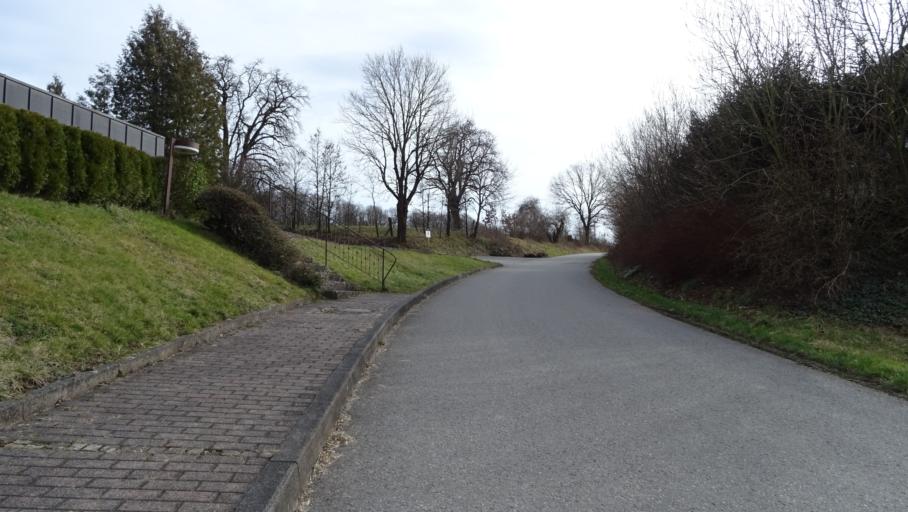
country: DE
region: Baden-Wuerttemberg
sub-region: Karlsruhe Region
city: Limbach
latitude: 49.4528
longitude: 9.2520
